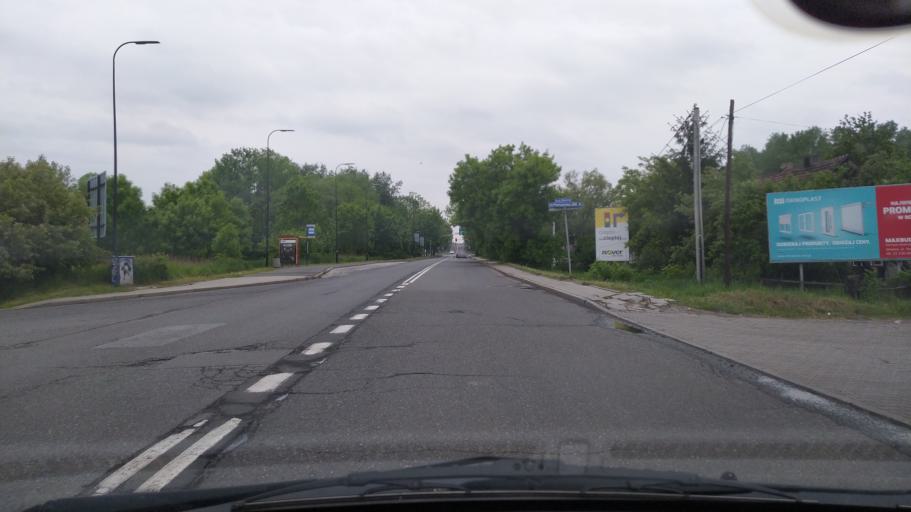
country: PL
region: Silesian Voivodeship
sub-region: Gliwice
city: Gliwice
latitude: 50.2749
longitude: 18.6991
